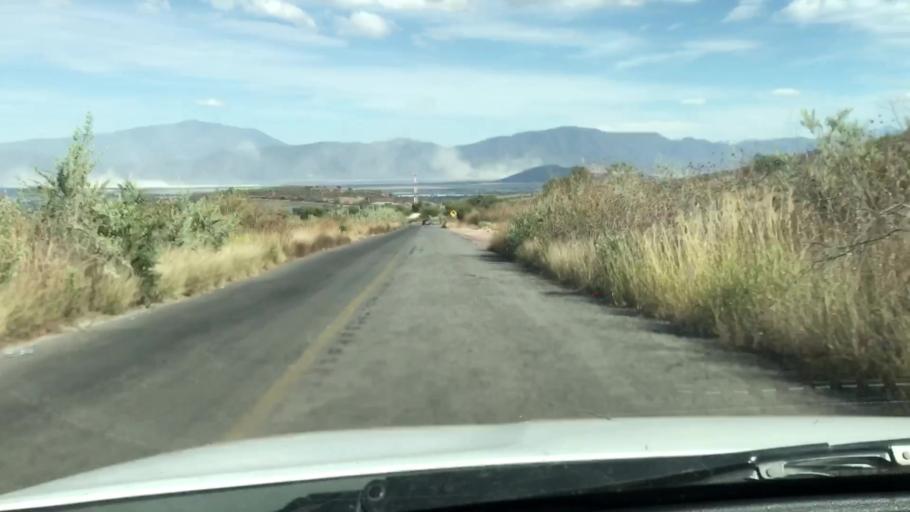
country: MX
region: Jalisco
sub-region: Zacoalco de Torres
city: Barranca de Otates (Barranca de Otatan)
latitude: 20.2563
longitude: -103.6709
